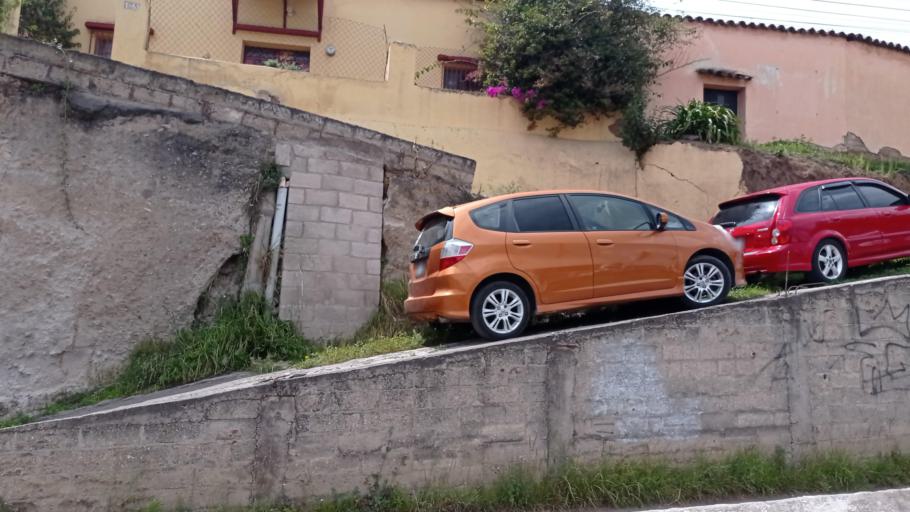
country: GT
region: Quetzaltenango
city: Quetzaltenango
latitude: 14.8459
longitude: -91.5015
